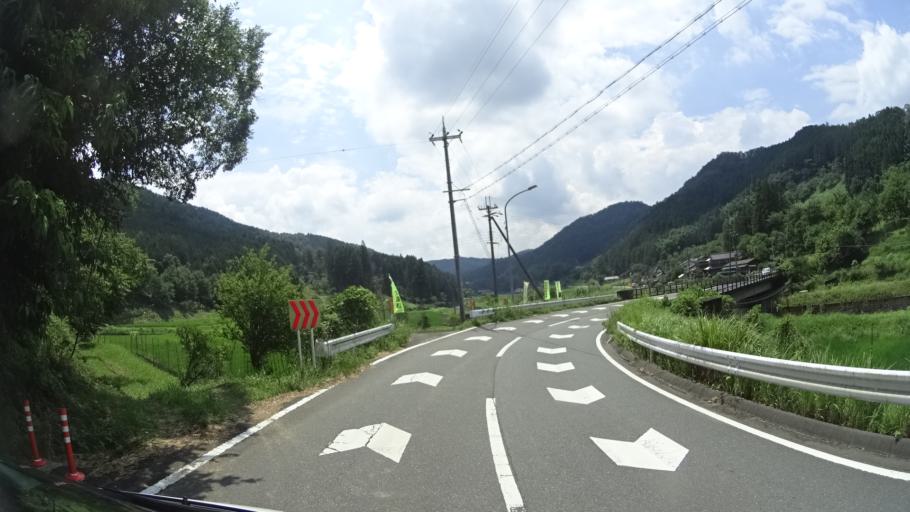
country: JP
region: Kyoto
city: Ayabe
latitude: 35.1956
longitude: 135.2650
